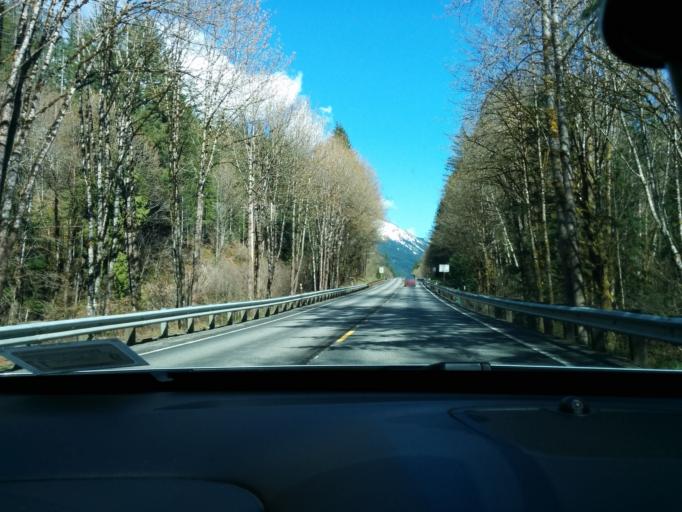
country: US
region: Washington
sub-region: Snohomish County
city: Gold Bar
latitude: 47.7153
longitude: -121.2615
